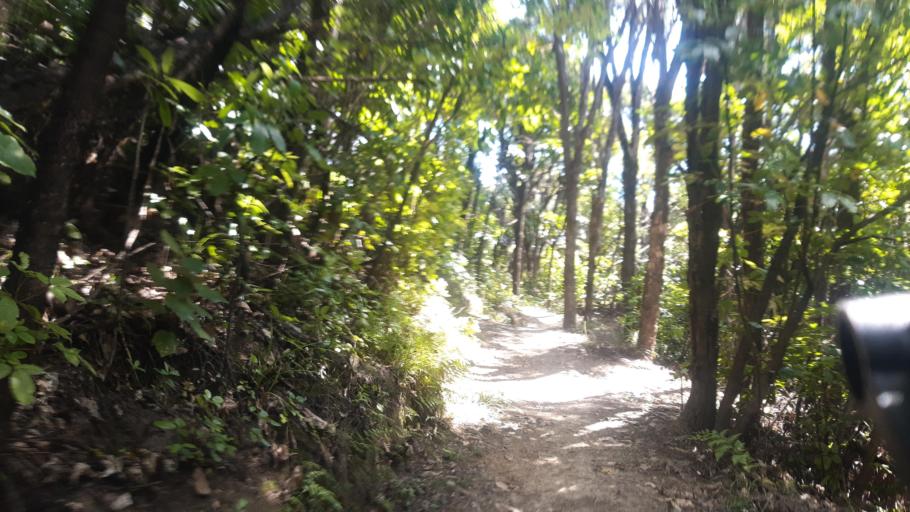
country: NZ
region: Marlborough
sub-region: Marlborough District
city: Picton
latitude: -41.2590
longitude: 174.0332
